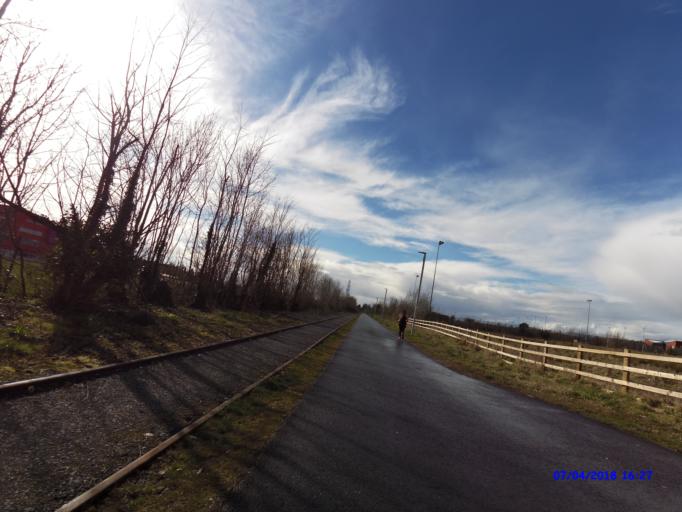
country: IE
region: Leinster
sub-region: An Iarmhi
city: Athlone
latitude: 53.4258
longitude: -7.9187
